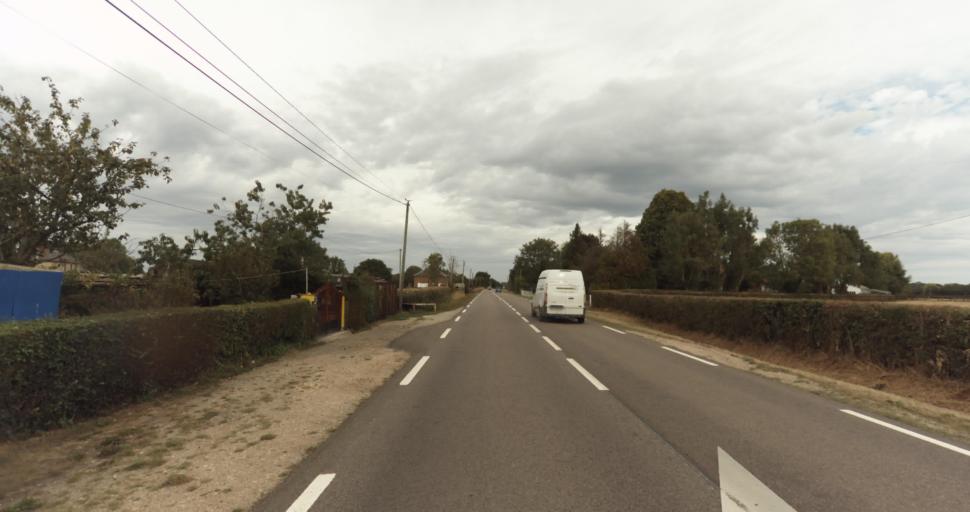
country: FR
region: Lower Normandy
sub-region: Departement de l'Orne
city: Vimoutiers
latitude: 48.9204
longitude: 0.2291
